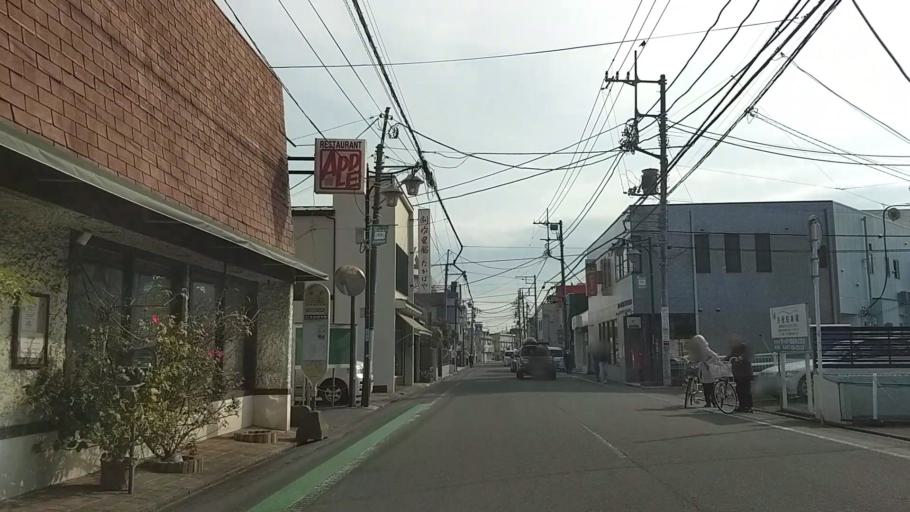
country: JP
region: Kanagawa
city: Chigasaki
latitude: 35.3278
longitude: 139.4078
